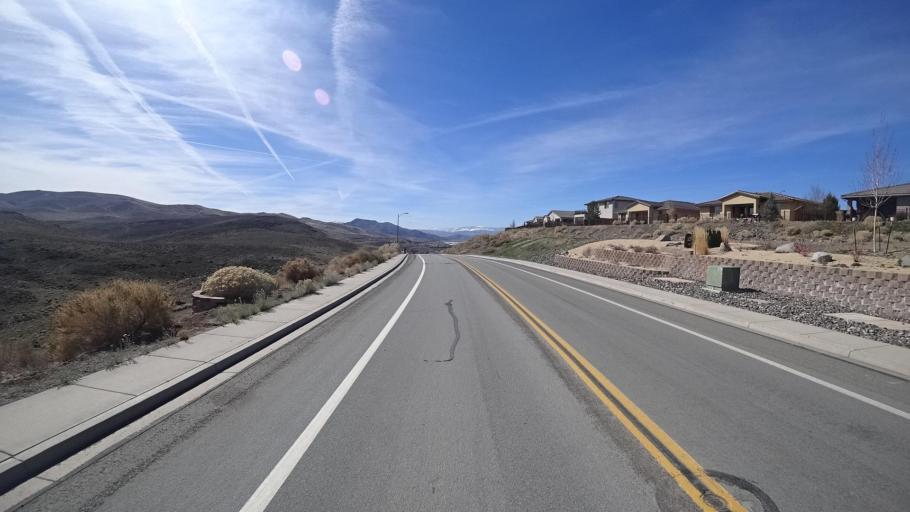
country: US
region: Nevada
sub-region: Washoe County
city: Spanish Springs
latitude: 39.5788
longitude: -119.6882
